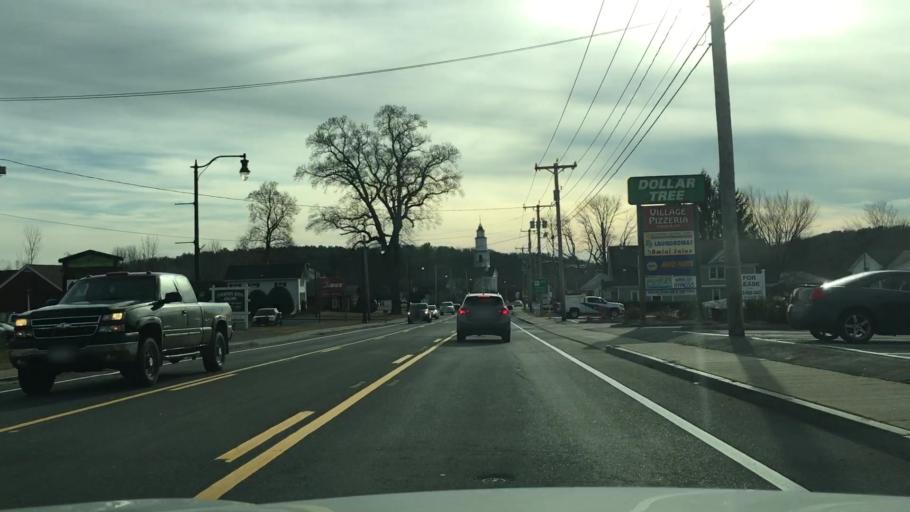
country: US
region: Massachusetts
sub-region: Hampden County
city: Southwick
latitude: 42.0577
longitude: -72.7679
